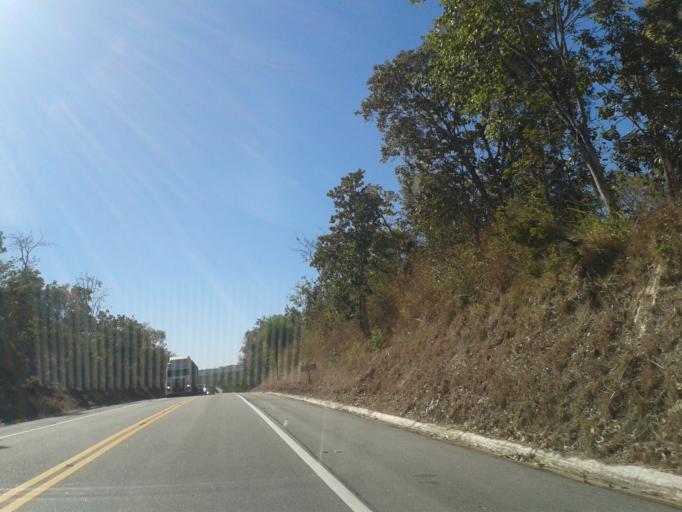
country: BR
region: Goias
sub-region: Goias
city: Goias
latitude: -15.7260
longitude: -50.1864
